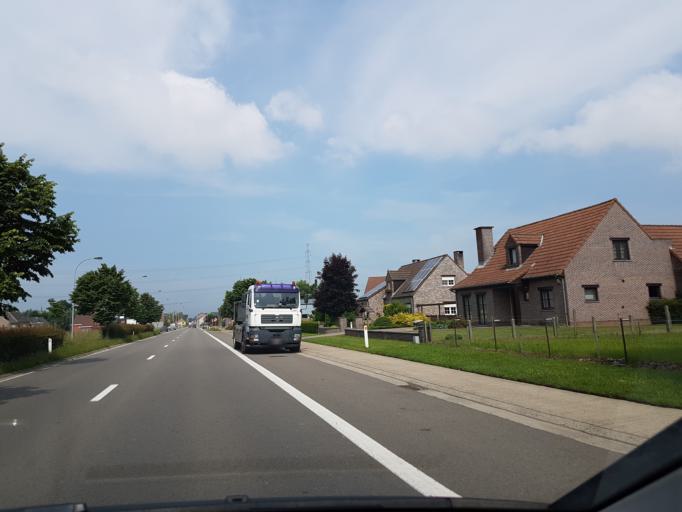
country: BE
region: Flanders
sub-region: Provincie Vlaams-Brabant
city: Merchtem
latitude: 50.9572
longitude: 4.2494
